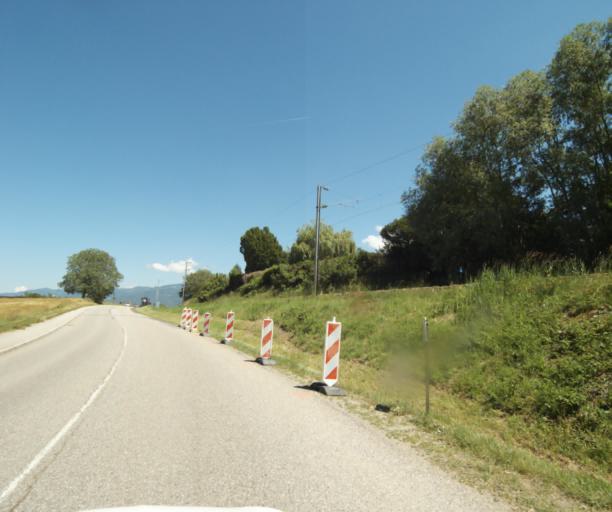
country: FR
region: Rhone-Alpes
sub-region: Departement de la Haute-Savoie
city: Bons-en-Chablais
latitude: 46.2713
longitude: 6.3537
